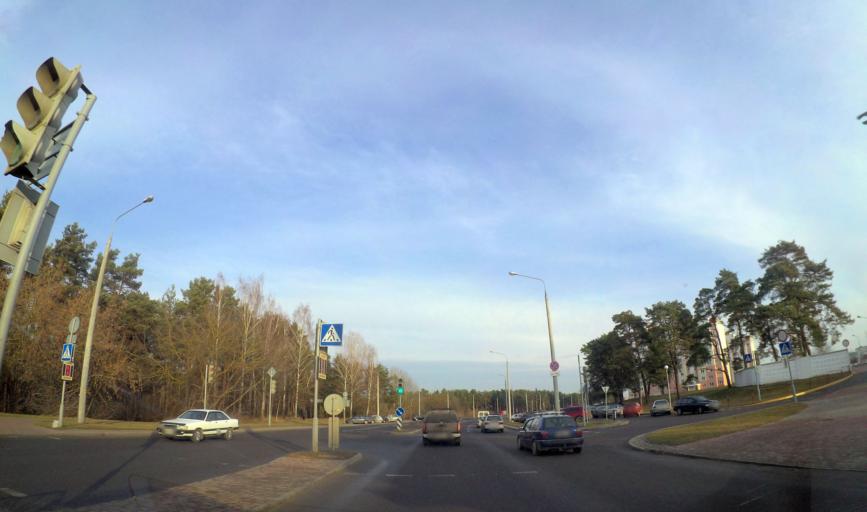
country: BY
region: Grodnenskaya
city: Hrodna
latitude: 53.6748
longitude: 23.7963
